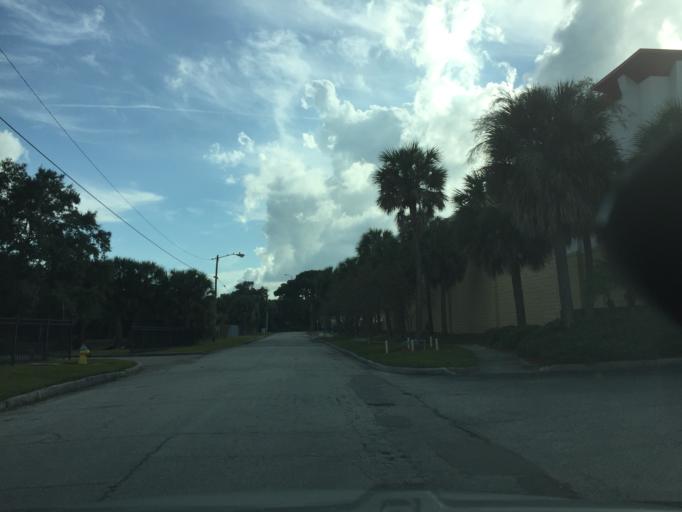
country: US
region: Florida
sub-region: Hillsborough County
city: Tampa
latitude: 27.9365
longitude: -82.4810
